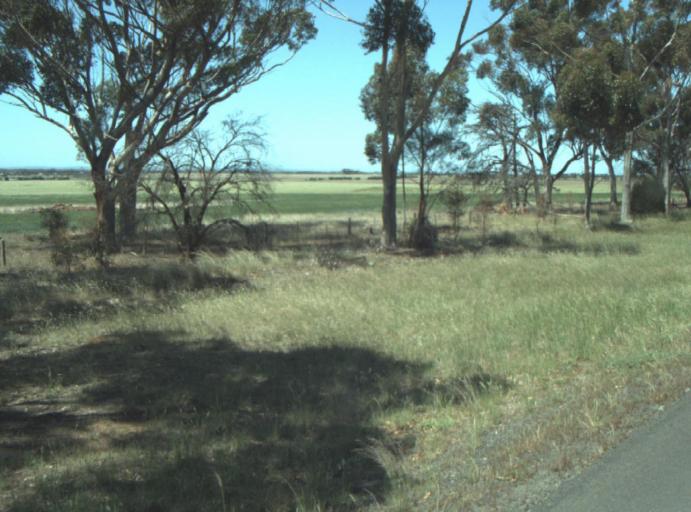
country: AU
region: Victoria
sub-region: Greater Geelong
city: Lara
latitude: -37.9572
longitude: 144.3518
